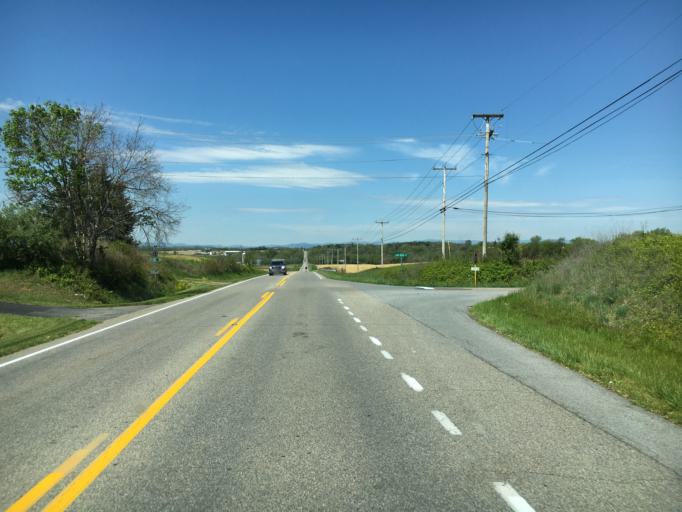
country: US
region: Virginia
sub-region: Rockingham County
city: Grottoes
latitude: 38.2659
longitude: -78.8516
